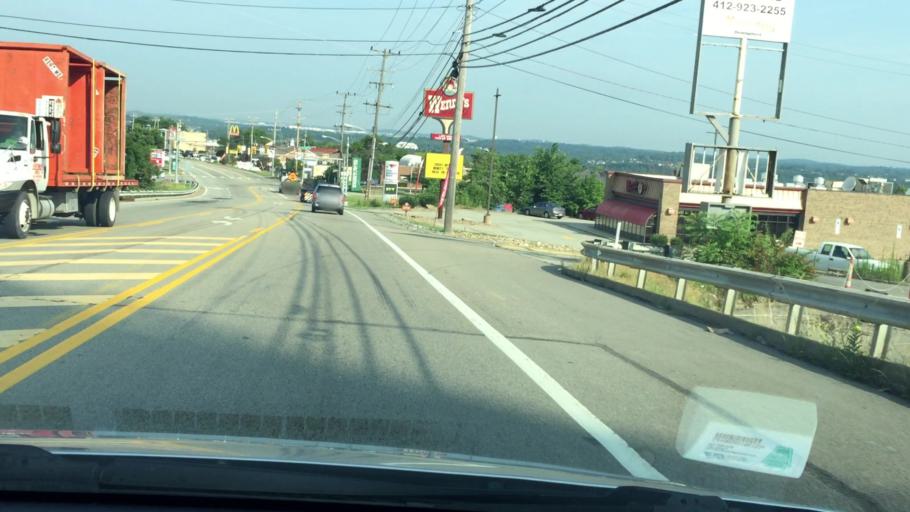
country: US
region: Pennsylvania
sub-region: Allegheny County
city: Rennerdale
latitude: 40.4469
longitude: -80.1531
